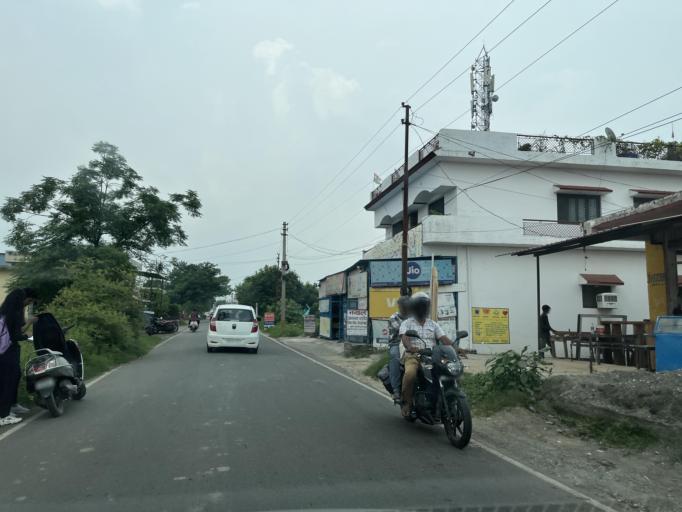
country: IN
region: Uttarakhand
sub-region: Naini Tal
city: Haldwani
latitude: 29.1949
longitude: 79.4842
